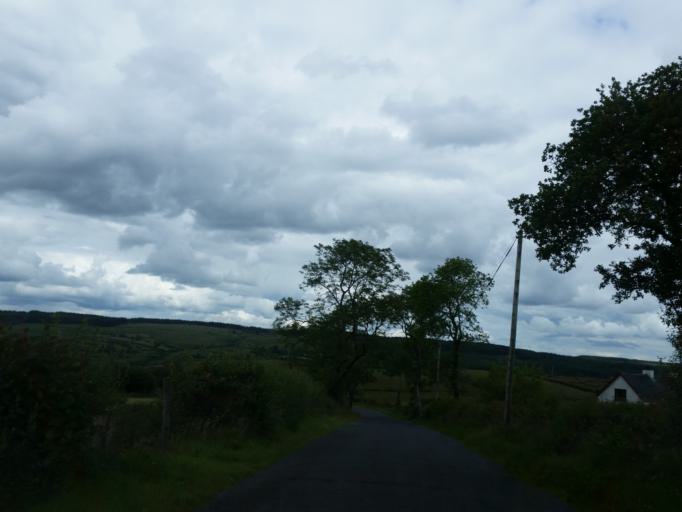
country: GB
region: Northern Ireland
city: Fivemiletown
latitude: 54.2811
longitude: -7.2768
